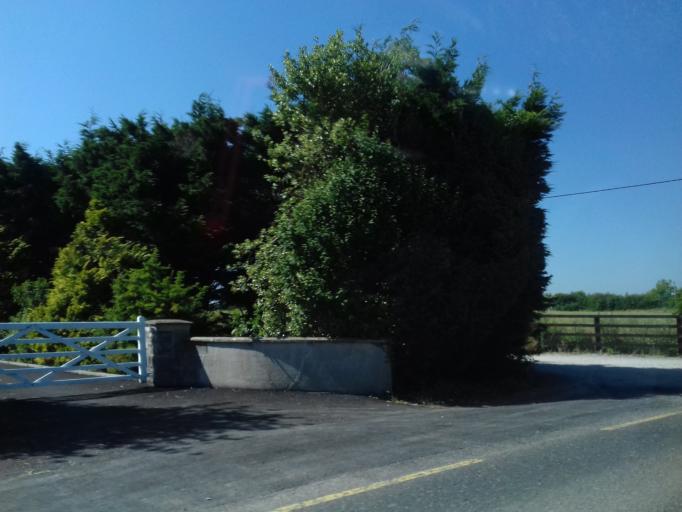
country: IE
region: Leinster
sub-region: Fingal County
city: Swords
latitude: 53.5032
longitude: -6.2689
